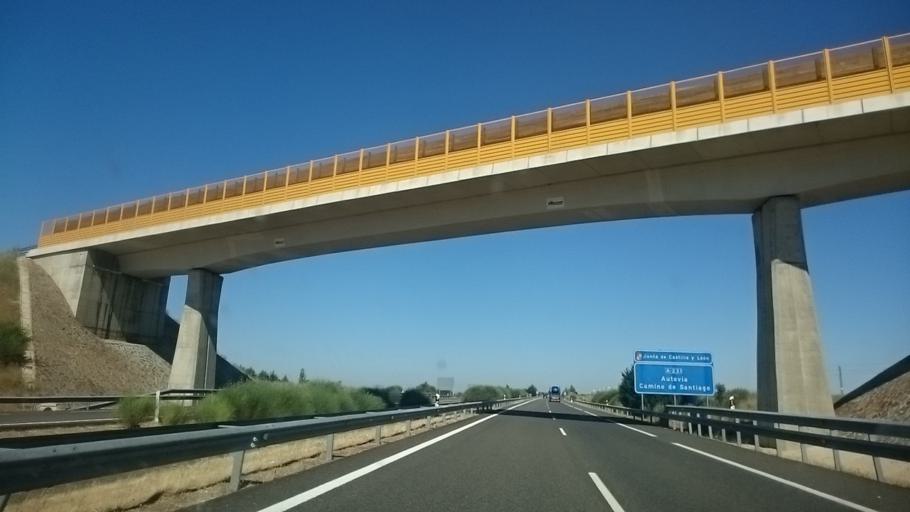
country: ES
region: Castille and Leon
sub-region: Provincia de Leon
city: Vallecillo
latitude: 42.4173
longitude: -5.2289
